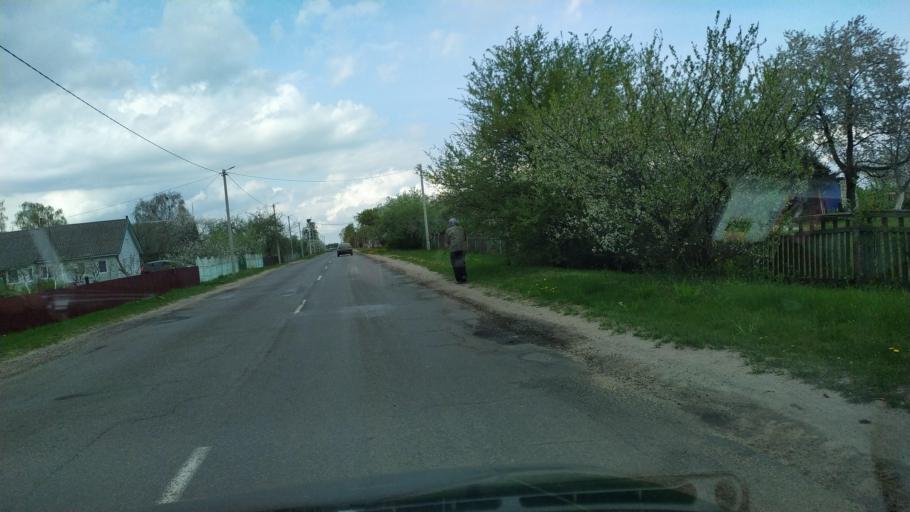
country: BY
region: Brest
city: Pruzhany
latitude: 52.5895
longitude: 24.4094
